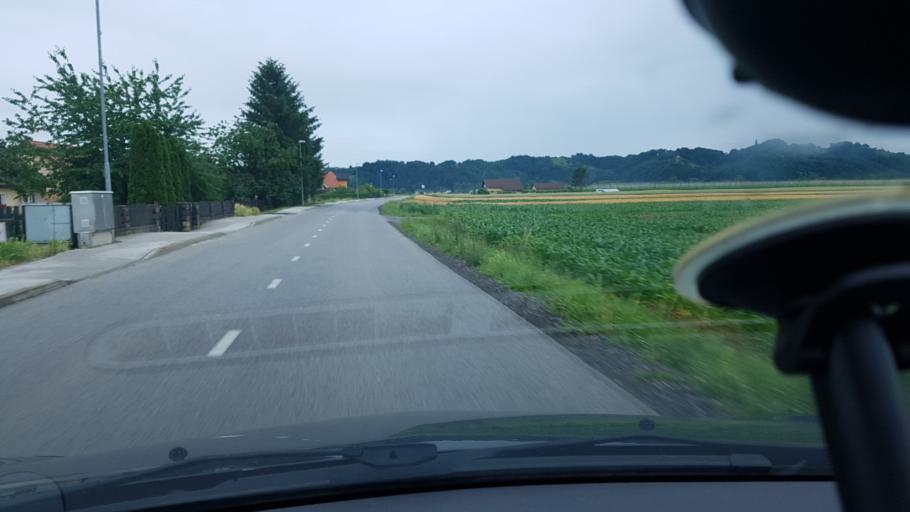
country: SI
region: Videm
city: Videm pri Ptuju
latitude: 46.3789
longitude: 15.8830
